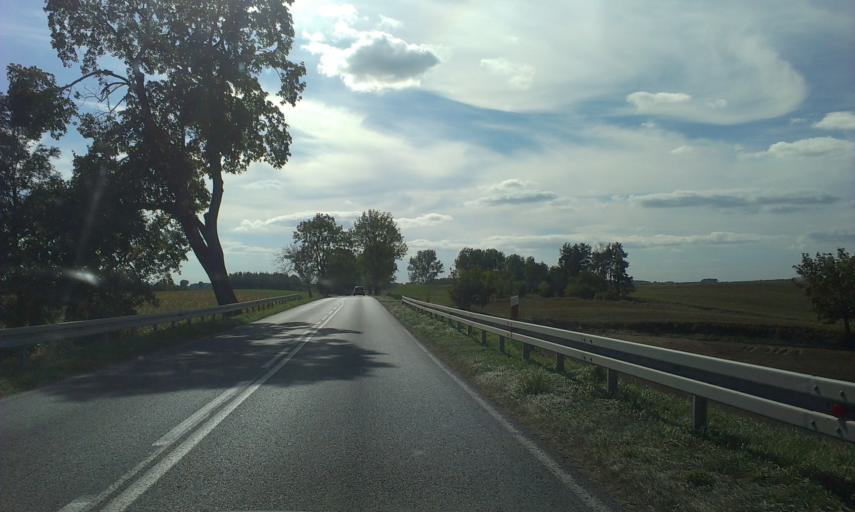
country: PL
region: Greater Poland Voivodeship
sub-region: Powiat pilski
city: Lobzenica
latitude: 53.2236
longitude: 17.2393
